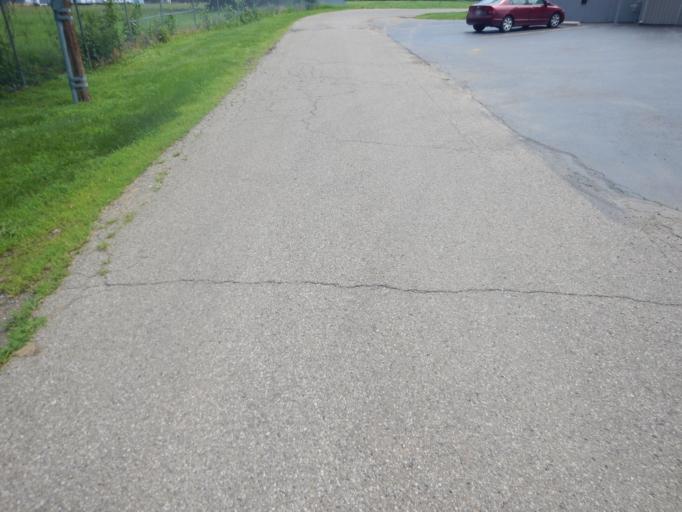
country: US
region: Ohio
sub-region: Muskingum County
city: North Zanesville
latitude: 39.9577
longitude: -82.0010
